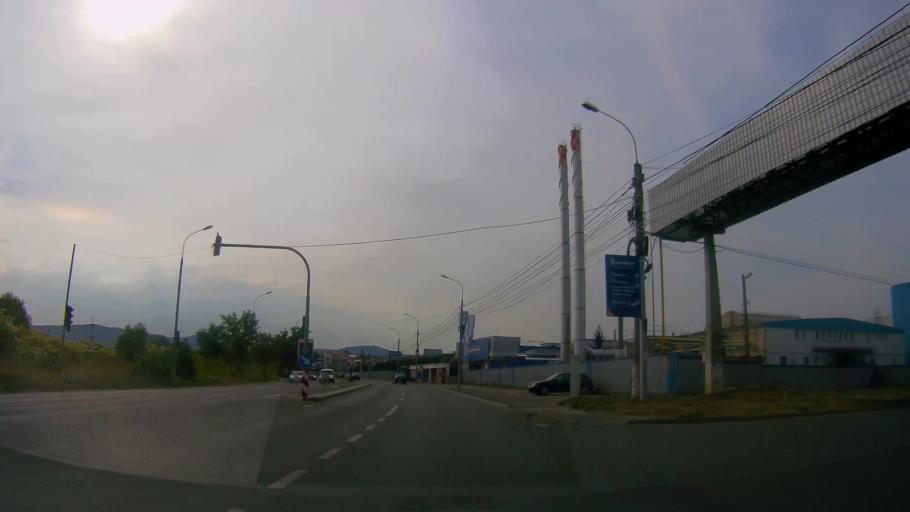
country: RO
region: Salaj
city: Zalau
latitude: 47.2094
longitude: 23.0444
